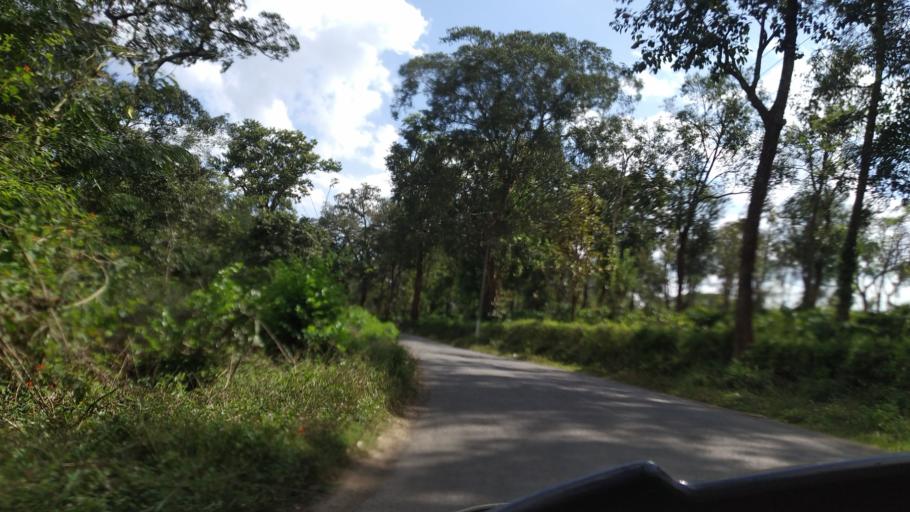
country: IN
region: Kerala
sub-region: Wayanad
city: Panamaram
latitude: 11.9551
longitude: 76.0629
